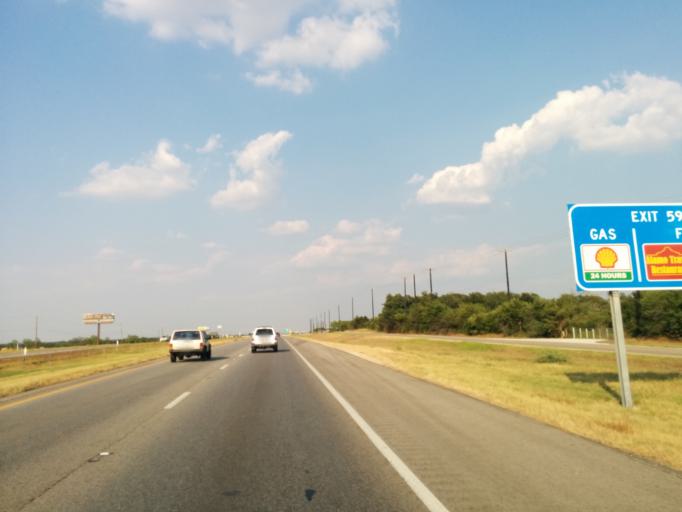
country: US
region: Texas
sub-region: Guadalupe County
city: Schertz
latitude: 29.4847
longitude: -98.2329
